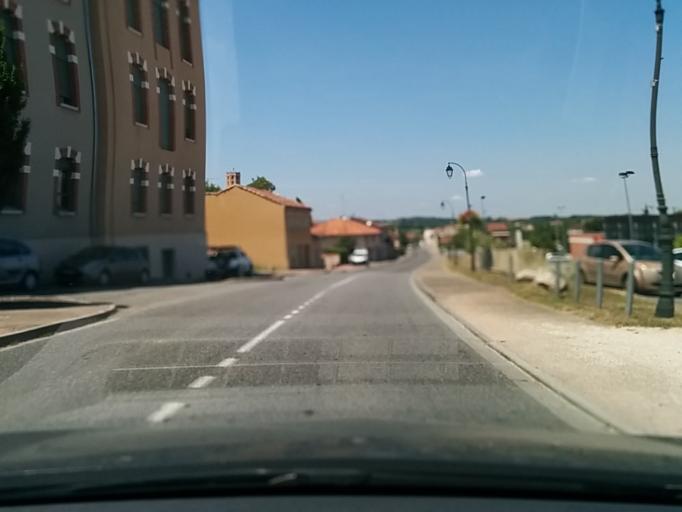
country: FR
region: Midi-Pyrenees
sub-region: Departement du Gers
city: Gimont
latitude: 43.6249
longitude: 0.8804
